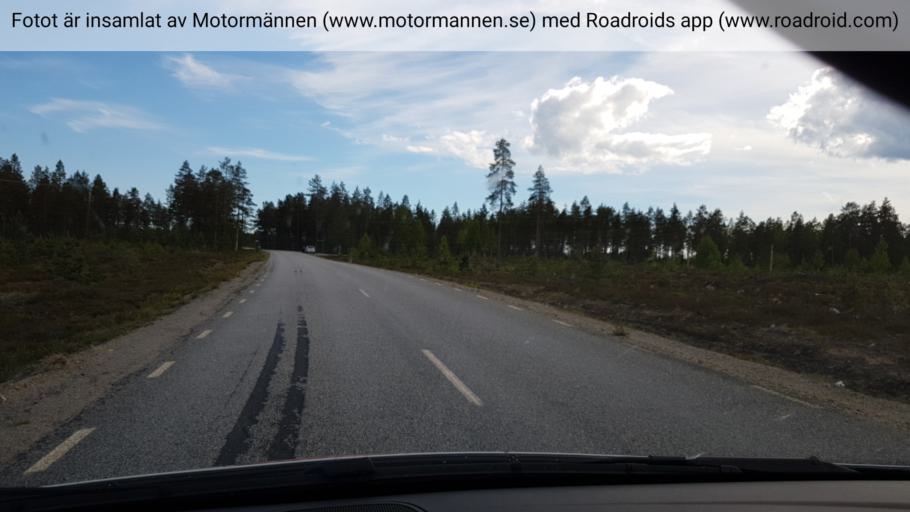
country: SE
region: Vaesterbotten
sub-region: Umea Kommun
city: Saevar
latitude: 63.9846
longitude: 20.5032
